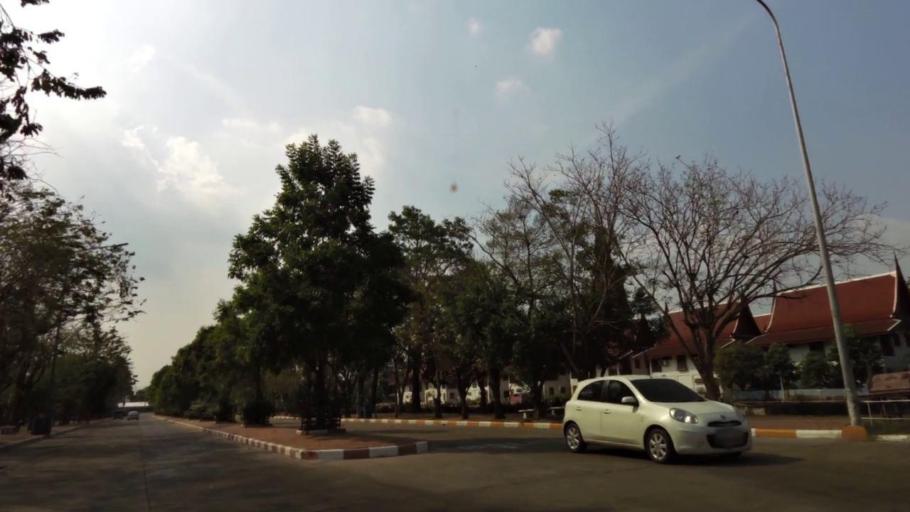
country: TH
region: Phra Nakhon Si Ayutthaya
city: Phra Nakhon Si Ayutthaya
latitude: 14.3442
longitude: 100.5940
